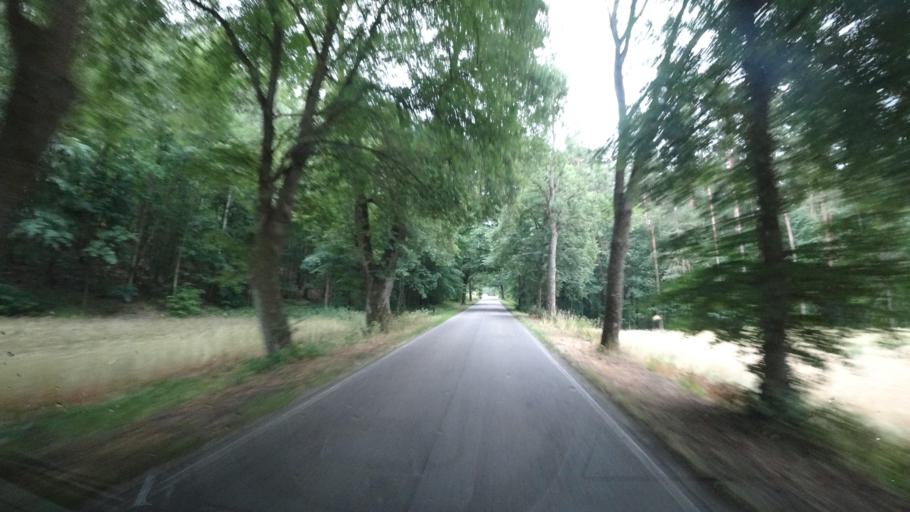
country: PL
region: Warmian-Masurian Voivodeship
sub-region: Powiat gizycki
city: Ryn
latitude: 53.8922
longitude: 21.5741
